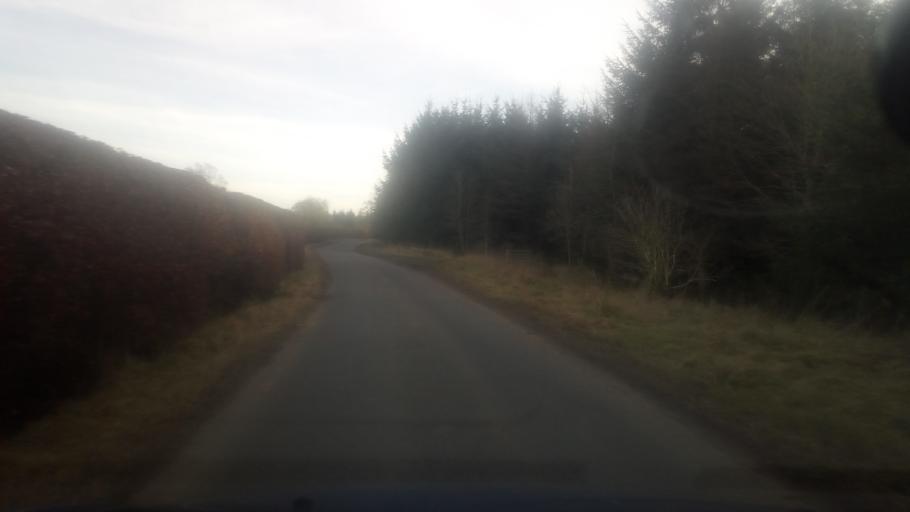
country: GB
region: Scotland
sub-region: The Scottish Borders
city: Jedburgh
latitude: 55.4164
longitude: -2.6183
